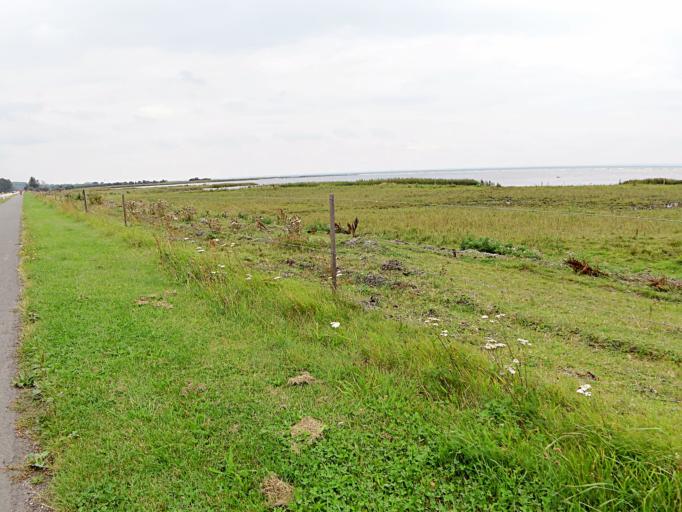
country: DK
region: Capital Region
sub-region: Fredensborg Kommune
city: Niva
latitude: 55.9239
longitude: 12.5168
